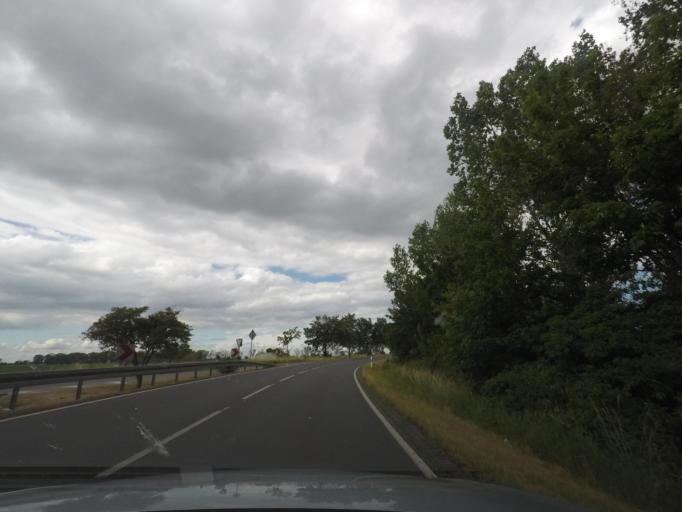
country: DE
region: Saxony-Anhalt
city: Ausleben
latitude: 52.0754
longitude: 11.0768
